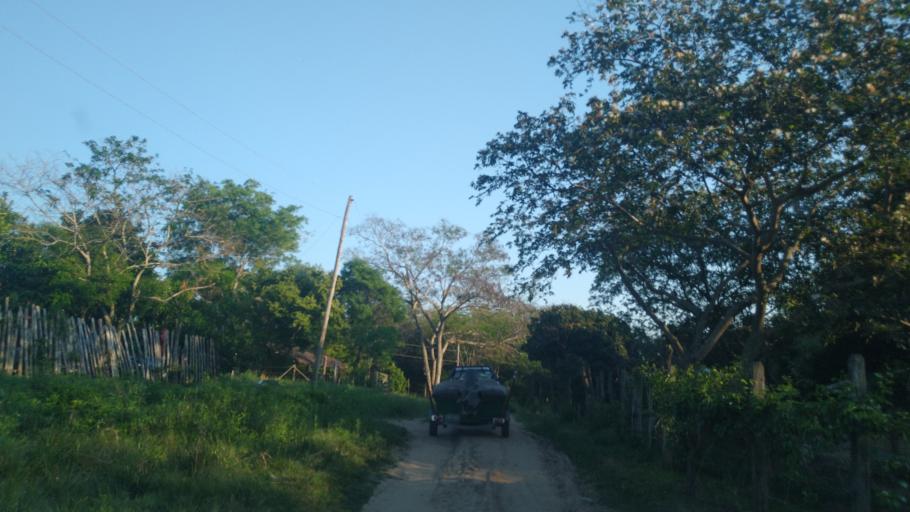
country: PY
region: Neembucu
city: Cerrito
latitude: -27.3704
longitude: -57.6565
